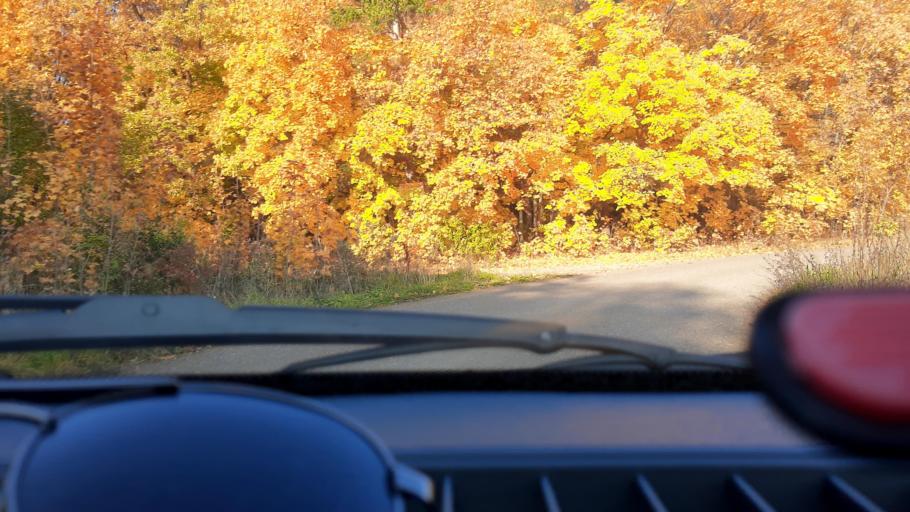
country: RU
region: Bashkortostan
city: Karmaskaly
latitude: 54.3773
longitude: 55.9104
